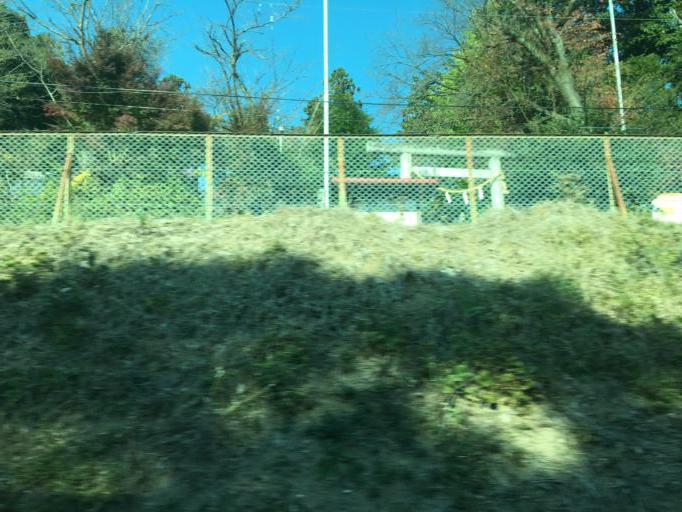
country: JP
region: Ibaraki
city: Iwase
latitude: 36.3555
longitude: 140.1423
